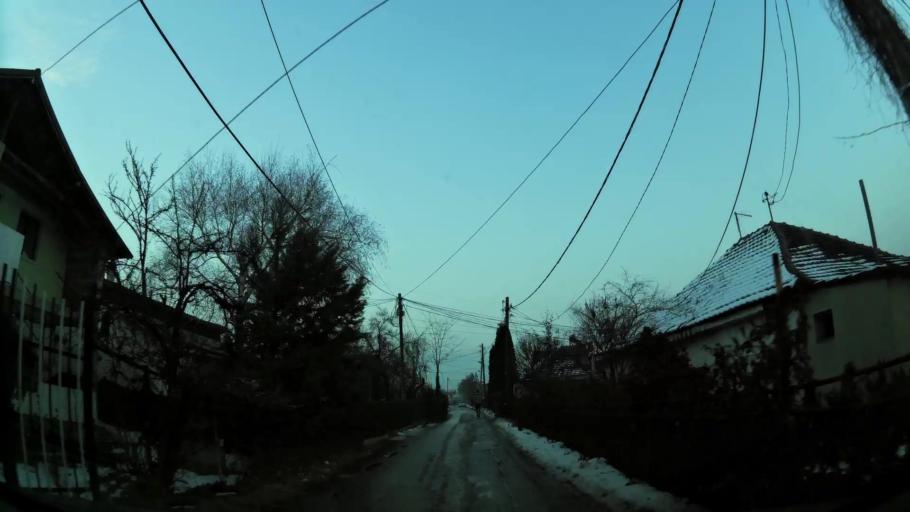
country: MK
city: Creshevo
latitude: 42.0010
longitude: 21.5035
